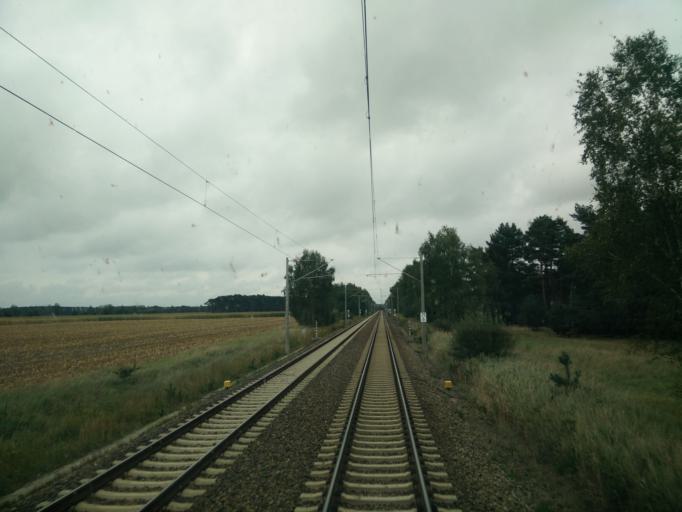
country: DE
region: Brandenburg
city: Luebben
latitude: 51.9548
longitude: 13.8405
